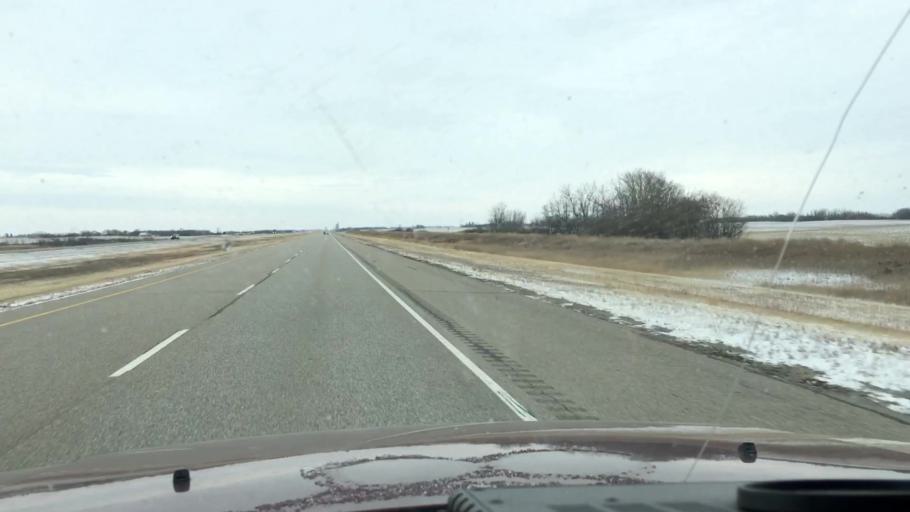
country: CA
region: Saskatchewan
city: Watrous
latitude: 51.3244
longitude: -106.0726
